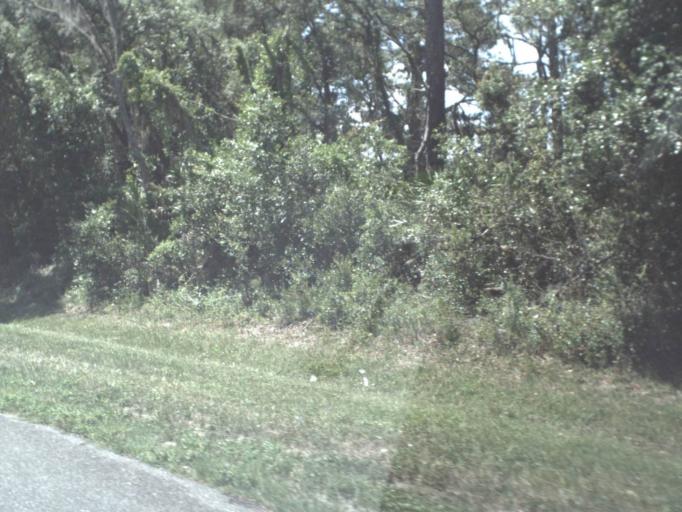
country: US
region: Florida
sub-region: Putnam County
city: Crescent City
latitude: 29.4687
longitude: -81.5290
